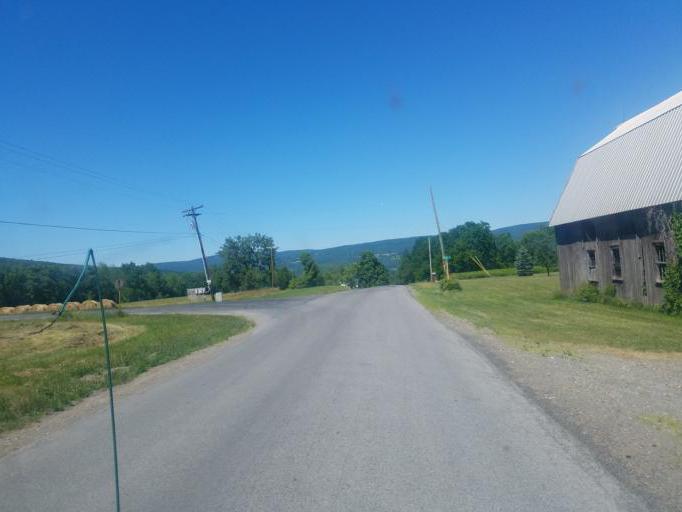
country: US
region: New York
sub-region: Ontario County
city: Canandaigua
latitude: 42.7256
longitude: -77.2933
